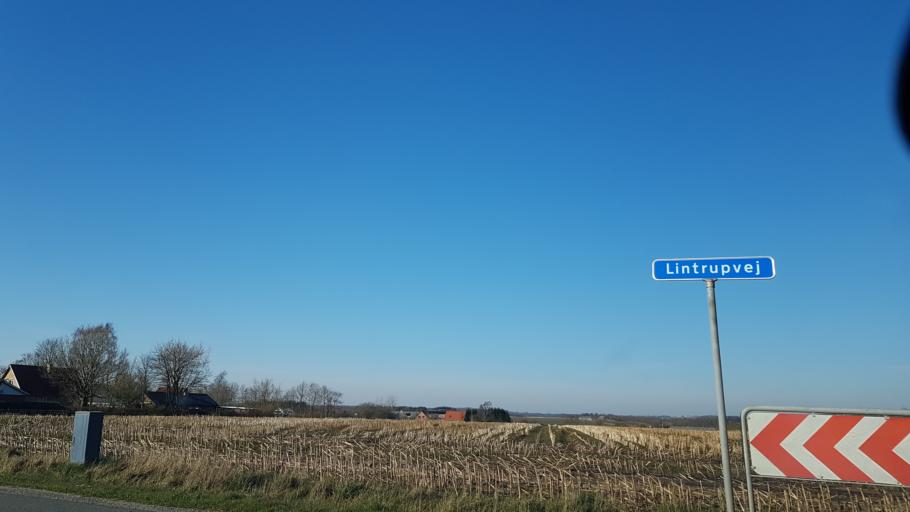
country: DK
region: South Denmark
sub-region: Vejen Kommune
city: Brorup
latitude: 55.4086
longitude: 8.9791
